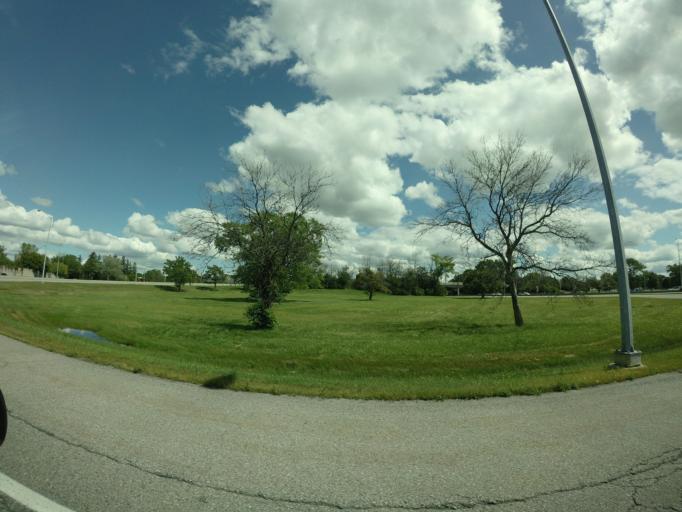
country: CA
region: Ontario
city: Bells Corners
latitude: 45.3614
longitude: -75.7705
